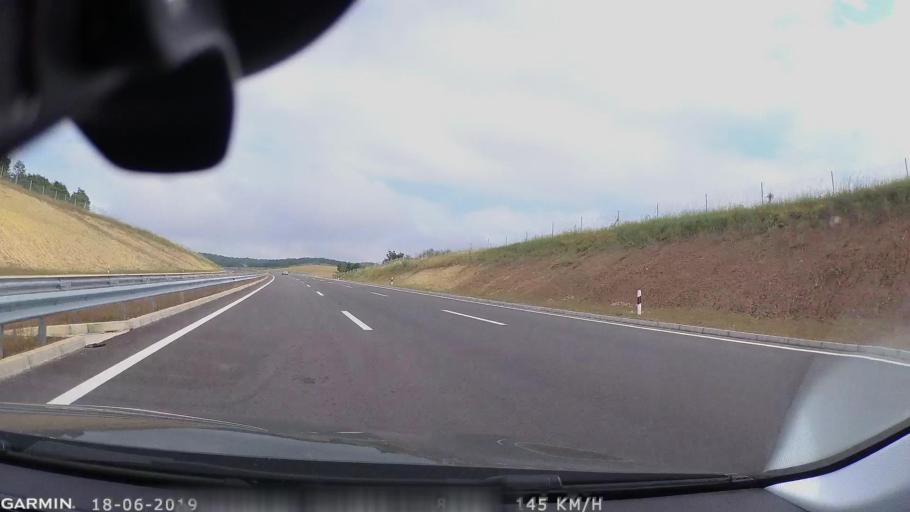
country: MK
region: Sveti Nikole
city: Gorobinci
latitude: 41.9182
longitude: 21.8756
